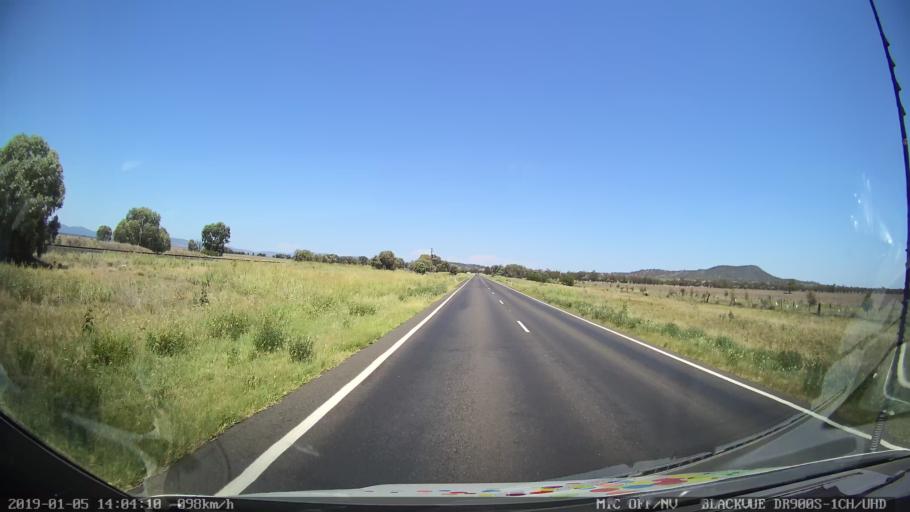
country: AU
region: New South Wales
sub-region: Gunnedah
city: Gunnedah
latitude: -31.1972
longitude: 150.3603
